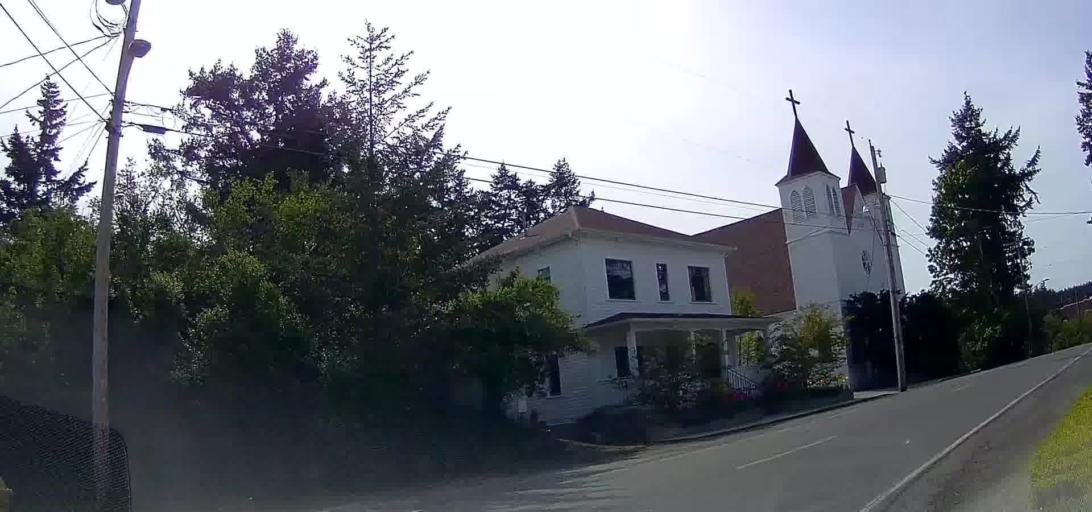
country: US
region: Washington
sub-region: Skagit County
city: Mount Vernon
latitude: 48.3880
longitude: -122.4952
